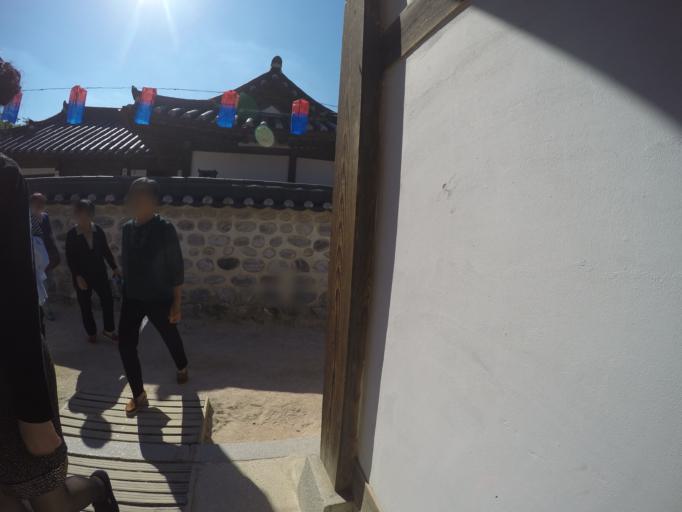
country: KR
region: Seoul
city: Seoul
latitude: 37.5590
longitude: 126.9946
